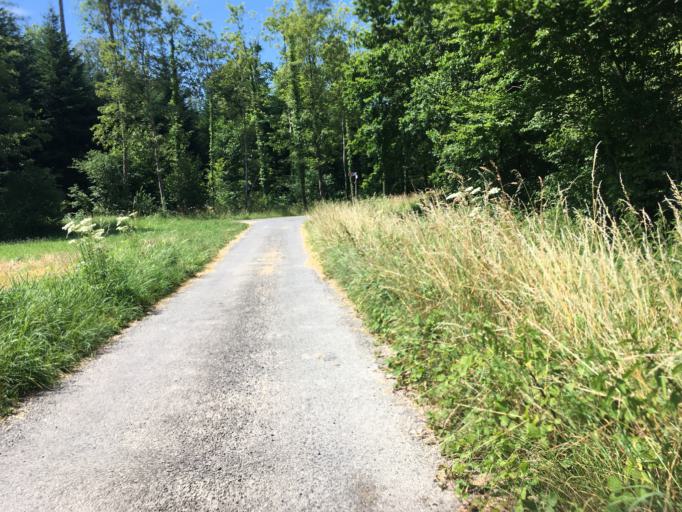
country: CH
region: Fribourg
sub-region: Broye District
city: Domdidier
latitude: 46.9343
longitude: 6.9922
